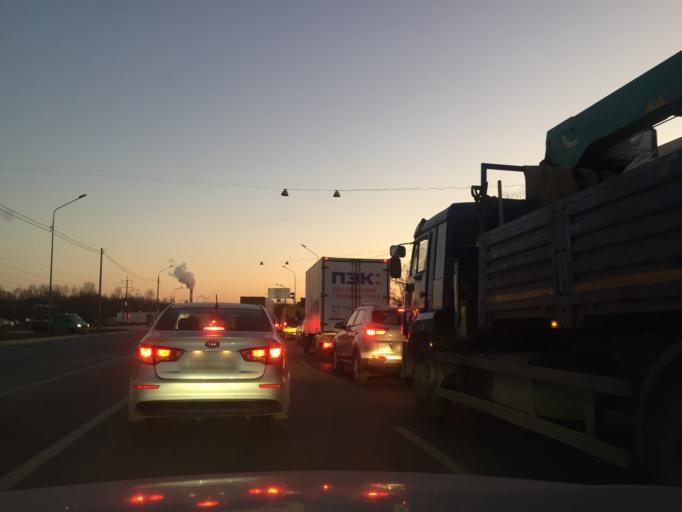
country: RU
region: St.-Petersburg
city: Obukhovo
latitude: 59.8536
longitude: 30.4252
